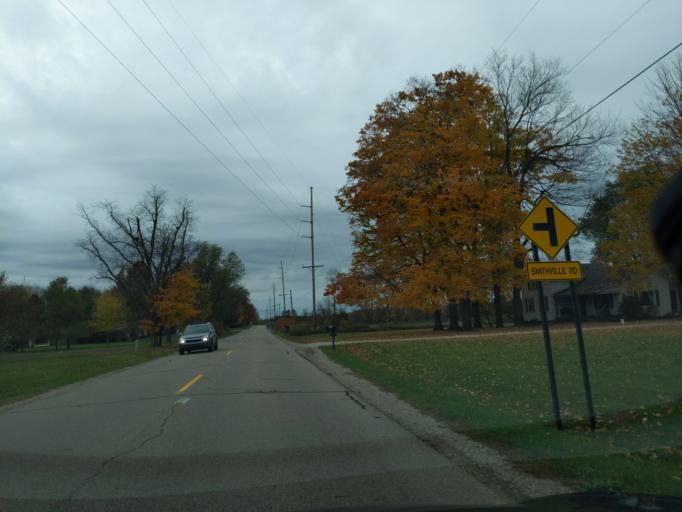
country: US
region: Michigan
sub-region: Eaton County
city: Eaton Rapids
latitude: 42.5239
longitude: -84.6287
